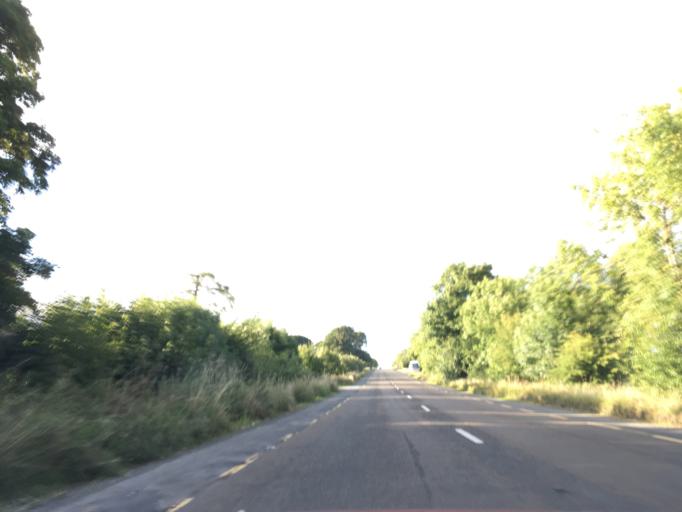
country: IE
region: Munster
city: Cashel
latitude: 52.4860
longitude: -7.8912
